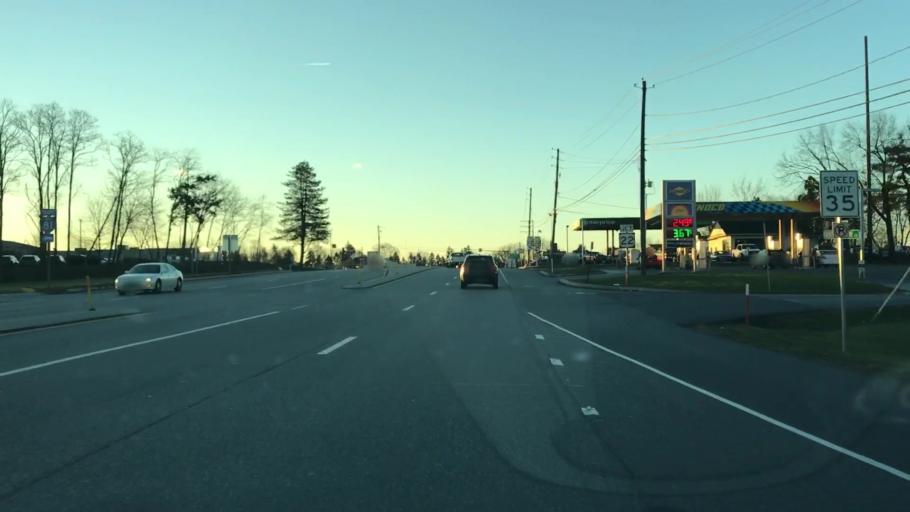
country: US
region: Pennsylvania
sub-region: Dauphin County
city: Paxtonia
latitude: 40.3245
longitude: -76.7907
